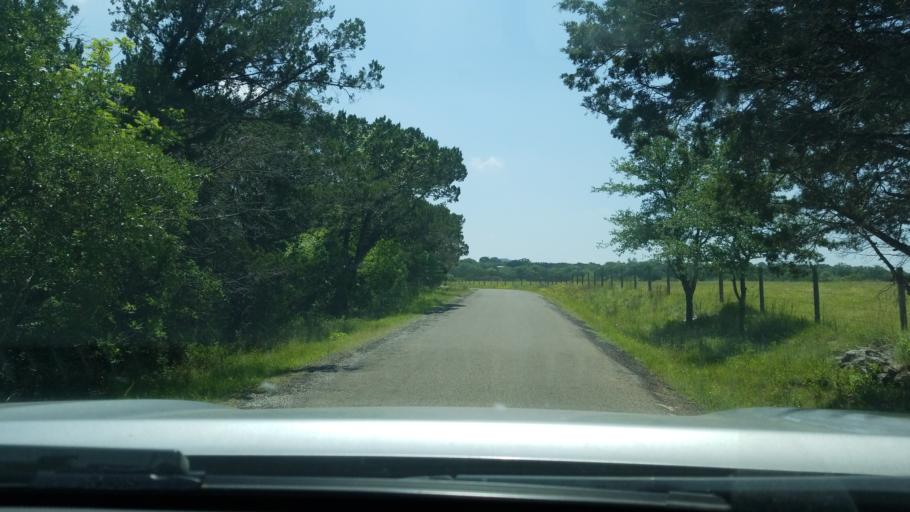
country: US
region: Texas
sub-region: Blanco County
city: Blanco
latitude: 30.0000
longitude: -98.4164
